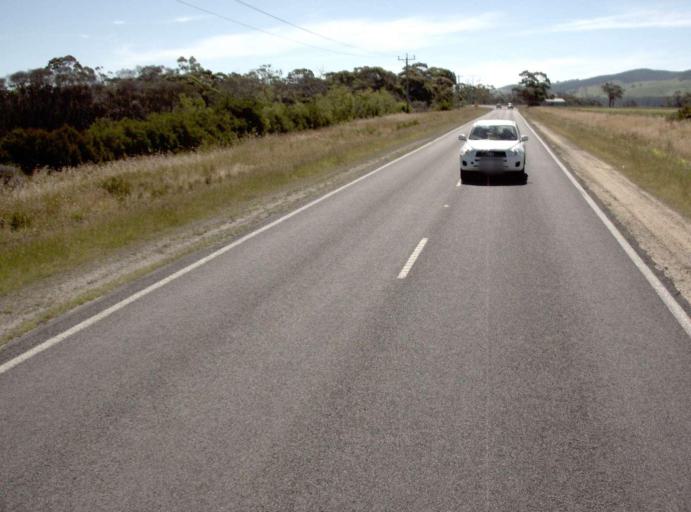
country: AU
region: Victoria
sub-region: Latrobe
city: Morwell
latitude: -38.6325
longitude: 146.5643
